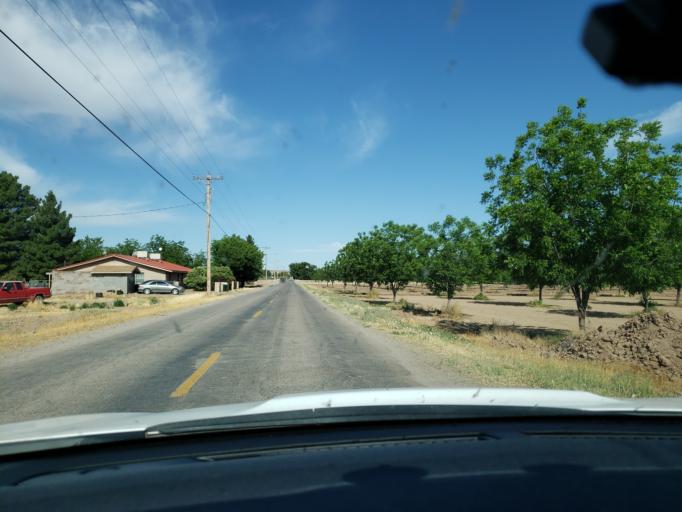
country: US
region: New Mexico
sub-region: Dona Ana County
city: Vado
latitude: 32.0826
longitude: -106.6867
